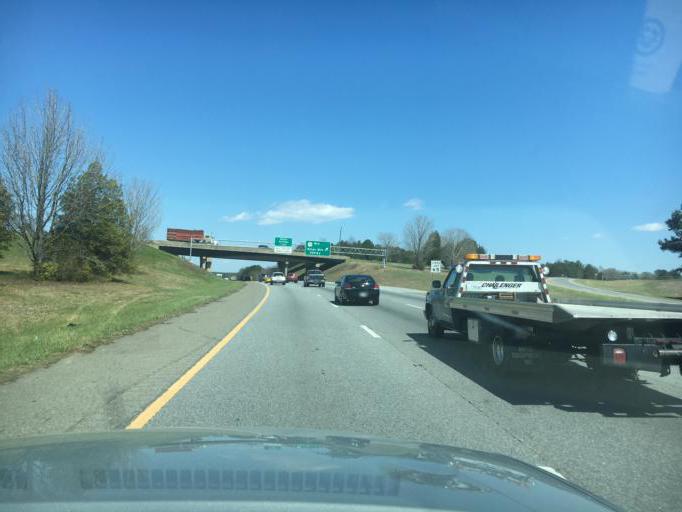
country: US
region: North Carolina
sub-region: Gaston County
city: Bessemer City
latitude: 35.2485
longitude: -81.3000
